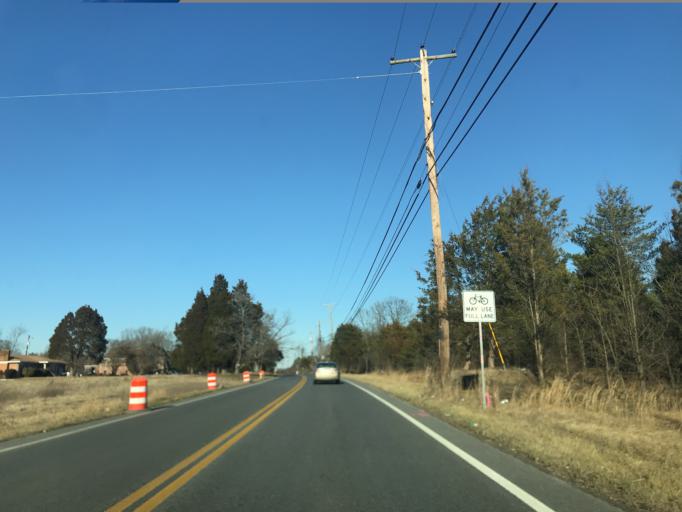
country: US
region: Maryland
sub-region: Prince George's County
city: Friendly
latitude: 38.7346
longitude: -76.9441
